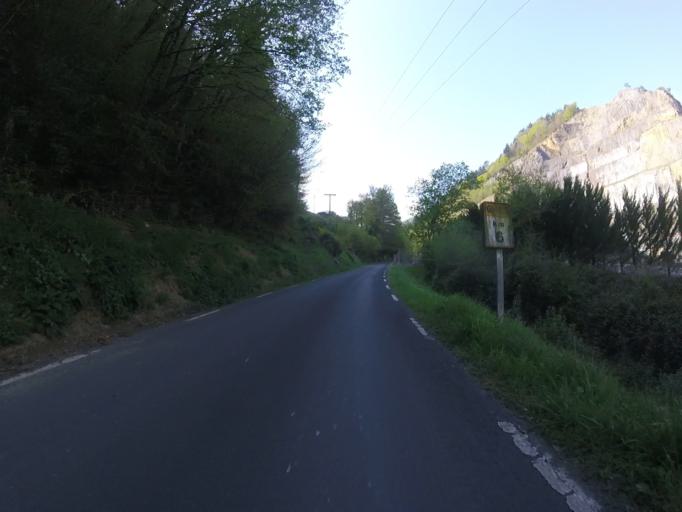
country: ES
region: Basque Country
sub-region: Provincia de Guipuzcoa
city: Azkoitia
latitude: 43.2381
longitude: -2.3233
